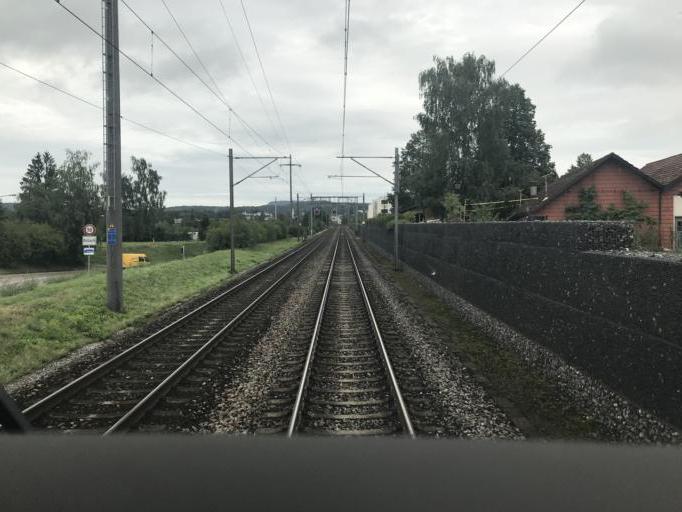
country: CH
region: Zurich
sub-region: Bezirk Buelach
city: Buelach / Niederflachs
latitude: 47.5123
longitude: 8.5230
